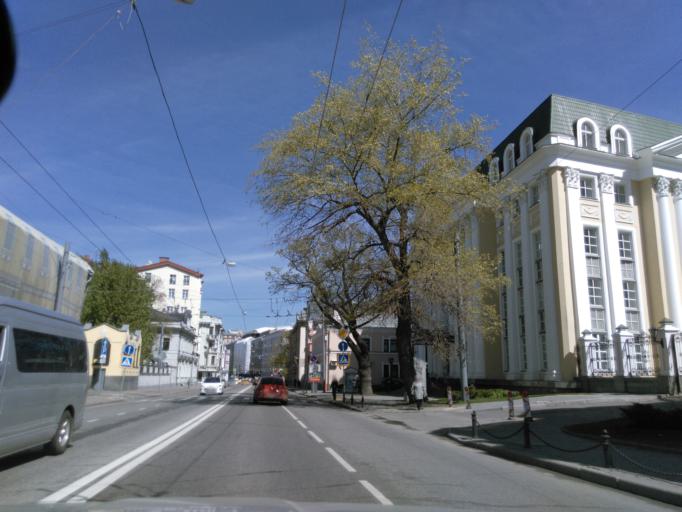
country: RU
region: Moscow
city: Moscow
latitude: 55.7401
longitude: 37.5968
